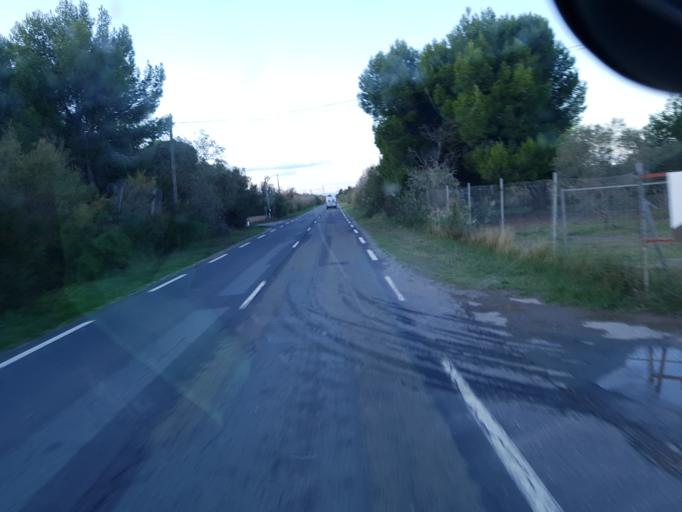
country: FR
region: Languedoc-Roussillon
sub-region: Departement de l'Aude
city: Port-la-Nouvelle
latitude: 43.0065
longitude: 3.0389
